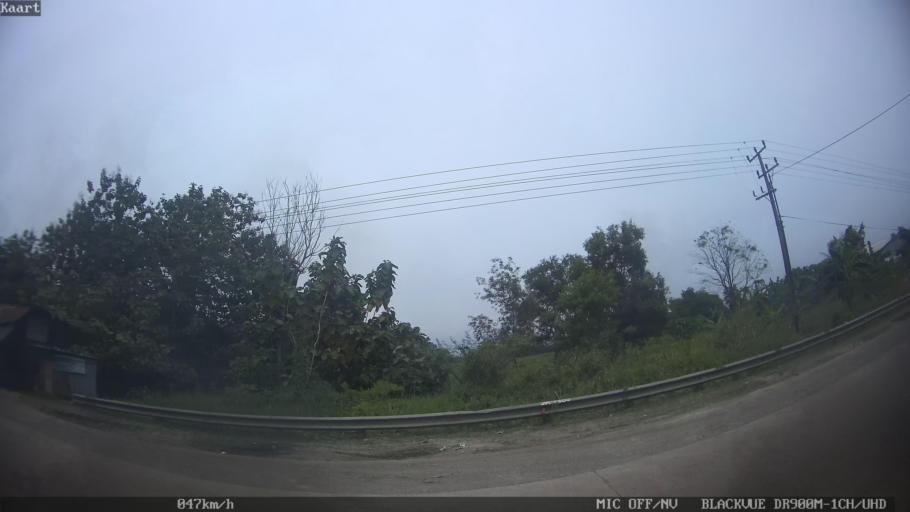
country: ID
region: Lampung
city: Bandarlampung
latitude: -5.4215
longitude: 105.2955
